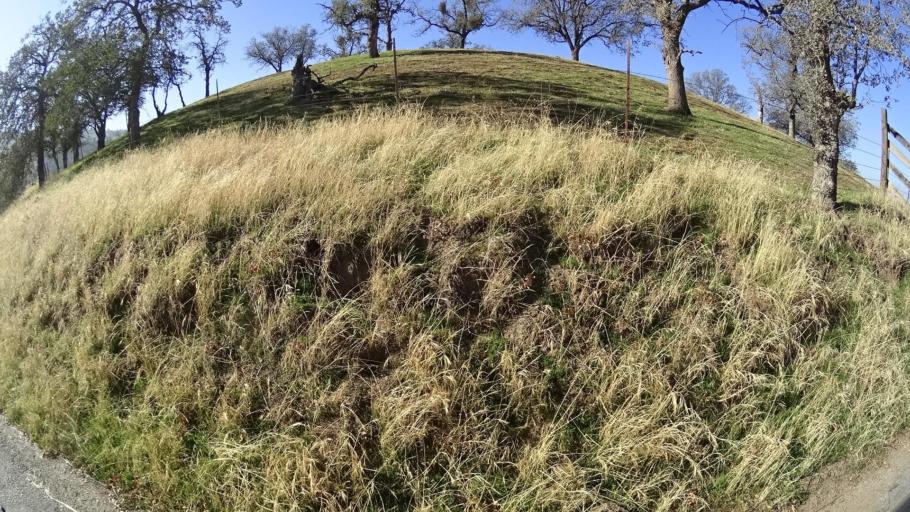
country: US
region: California
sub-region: Kern County
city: Alta Sierra
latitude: 35.7179
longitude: -118.8103
